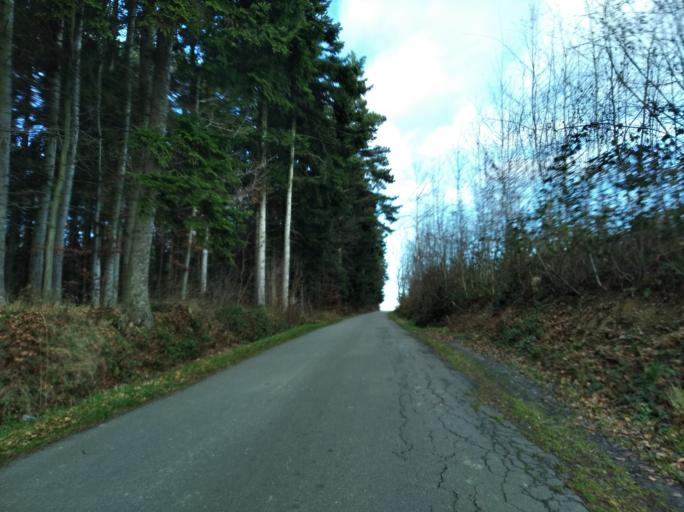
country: PL
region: Subcarpathian Voivodeship
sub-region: Powiat strzyzowski
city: Babica
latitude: 49.9086
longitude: 21.8496
